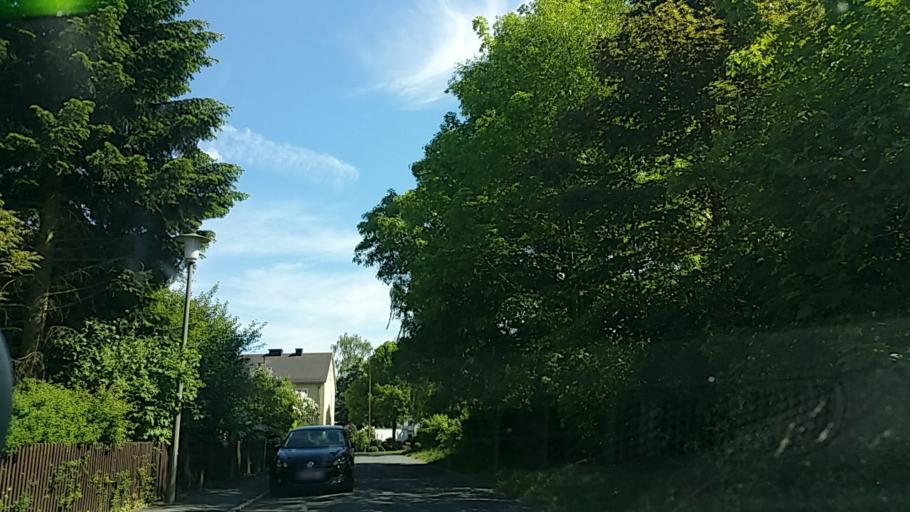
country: DE
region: Bavaria
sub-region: Upper Franconia
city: Schwarzenbach an der Saale
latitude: 50.2173
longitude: 11.9424
